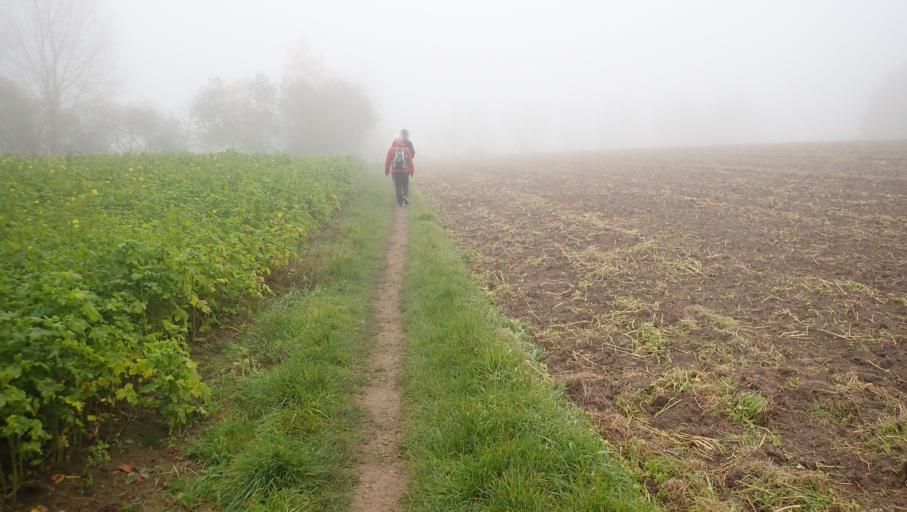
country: BE
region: Flanders
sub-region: Provincie Oost-Vlaanderen
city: Temse
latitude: 51.1187
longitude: 4.1827
